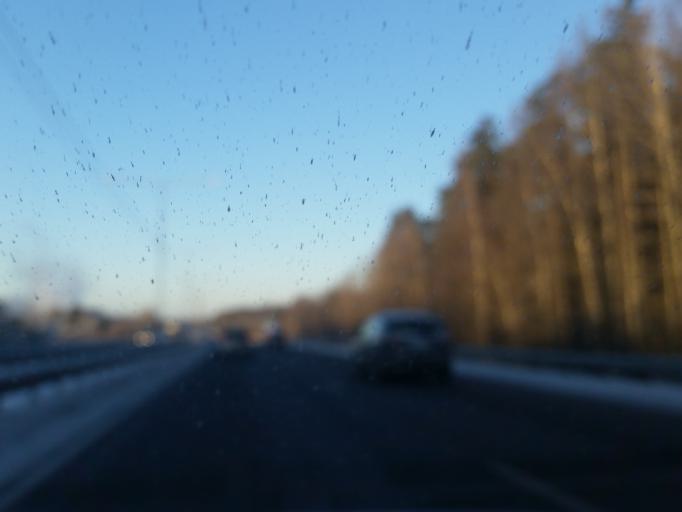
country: SE
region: Stockholm
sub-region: Sodertalje Kommun
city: Soedertaelje
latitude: 59.1824
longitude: 17.5911
